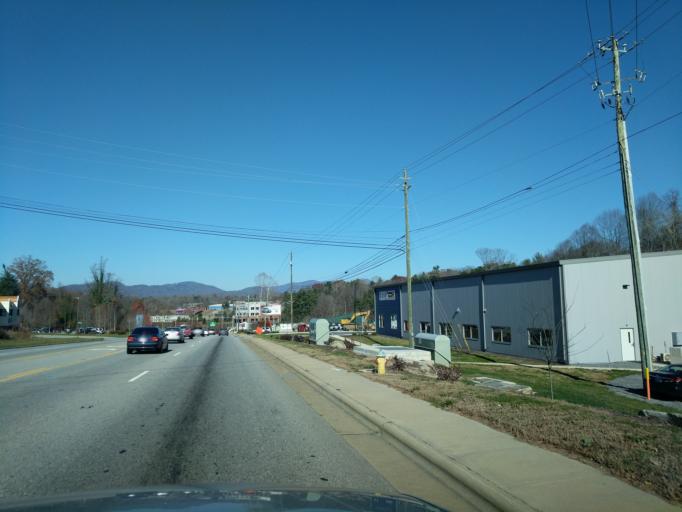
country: US
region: North Carolina
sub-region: Buncombe County
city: Biltmore Forest
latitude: 35.5497
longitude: -82.5206
